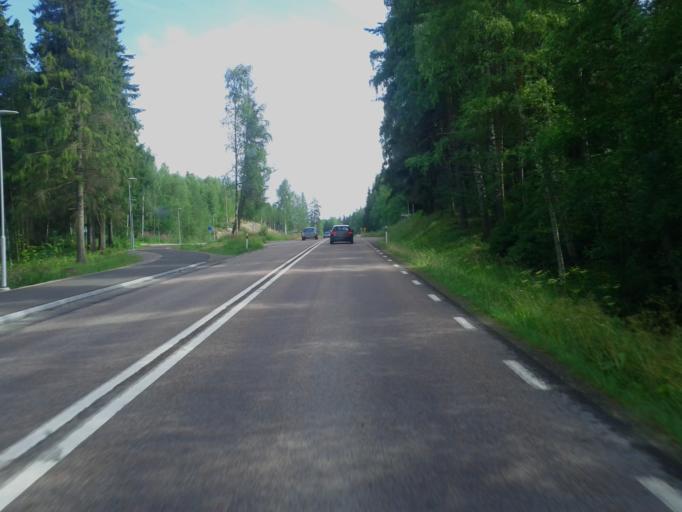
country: SE
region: Dalarna
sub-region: Faluns Kommun
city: Grycksbo
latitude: 60.6785
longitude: 15.5080
